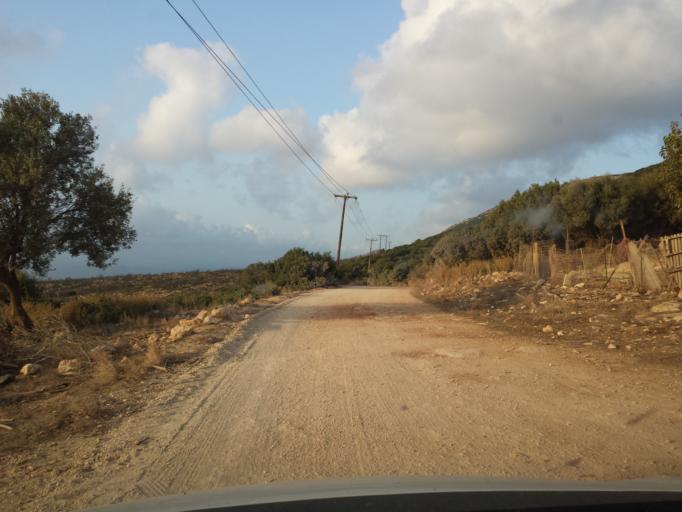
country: GR
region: Peloponnese
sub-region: Nomos Messinias
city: Pylos
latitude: 36.8884
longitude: 21.6871
